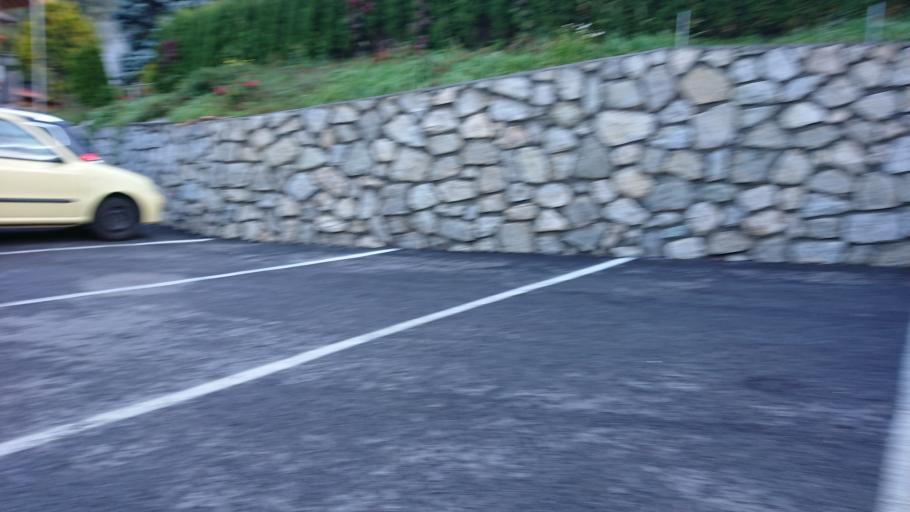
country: IT
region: Trentino-Alto Adige
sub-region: Bolzano
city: Campo di Trens
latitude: 46.8756
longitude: 11.4862
